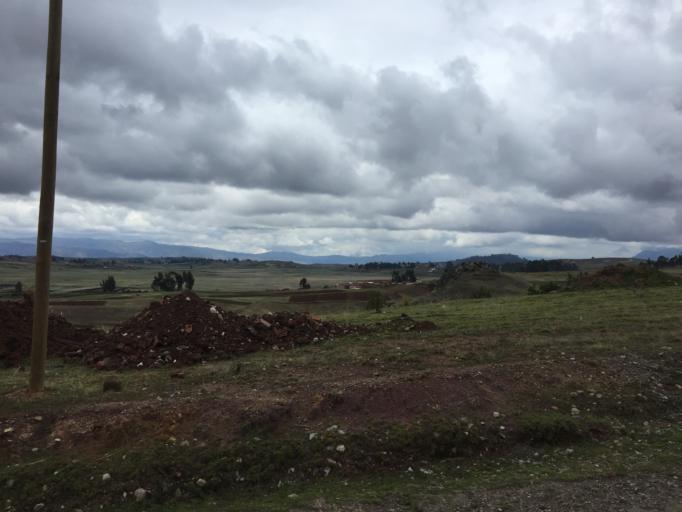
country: PE
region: Cusco
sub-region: Provincia de Urubamba
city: Chinchero
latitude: -13.3765
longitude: -72.0596
